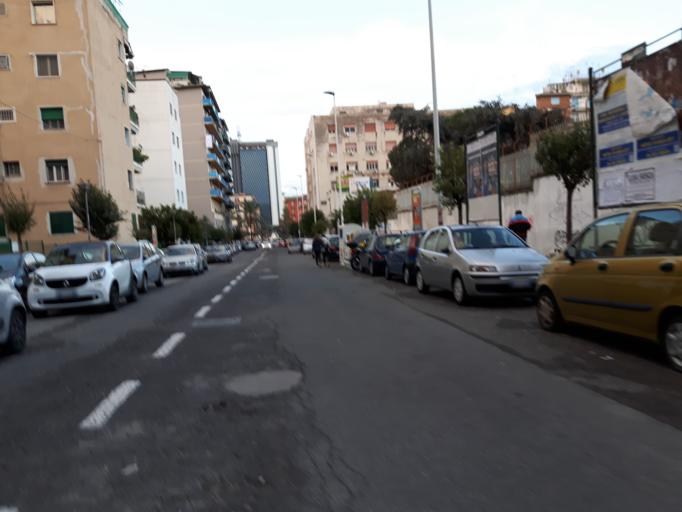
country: IT
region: Campania
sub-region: Provincia di Napoli
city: Napoli
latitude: 40.8597
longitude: 14.2714
